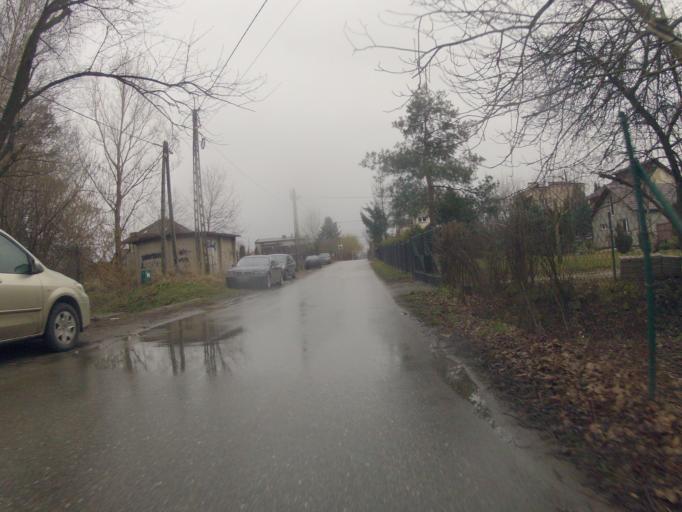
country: PL
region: Lesser Poland Voivodeship
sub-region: Powiat wielicki
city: Kokotow
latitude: 50.0588
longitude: 20.0454
